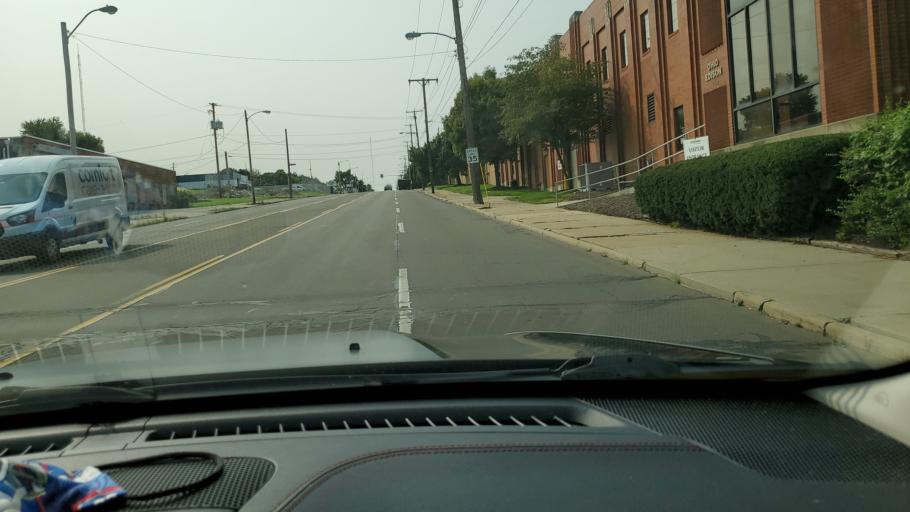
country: US
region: Ohio
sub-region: Mahoning County
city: Youngstown
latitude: 41.0919
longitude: -80.6464
